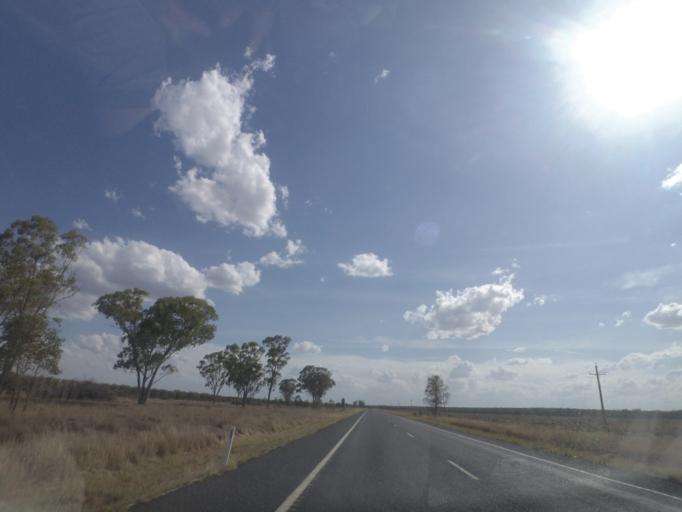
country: AU
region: New South Wales
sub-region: Moree Plains
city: Boggabilla
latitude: -28.5225
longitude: 150.9064
